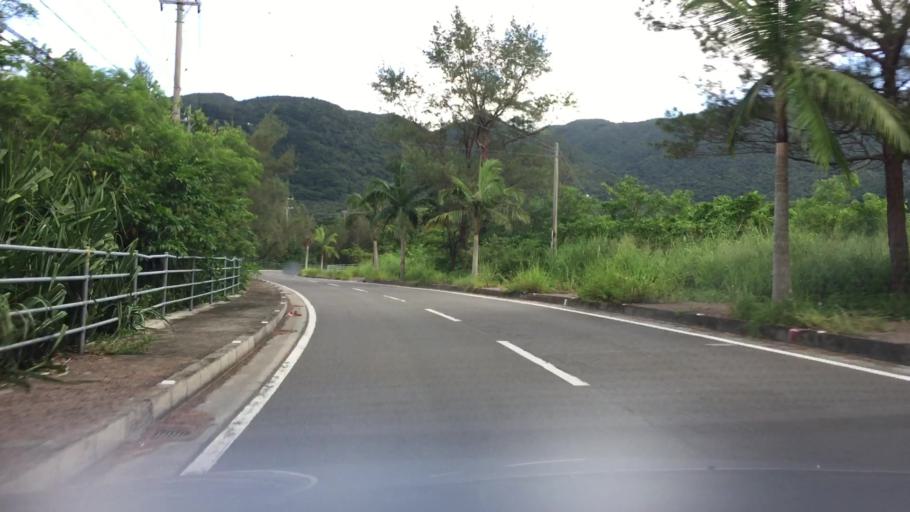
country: JP
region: Okinawa
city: Ishigaki
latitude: 24.4447
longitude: 124.1358
